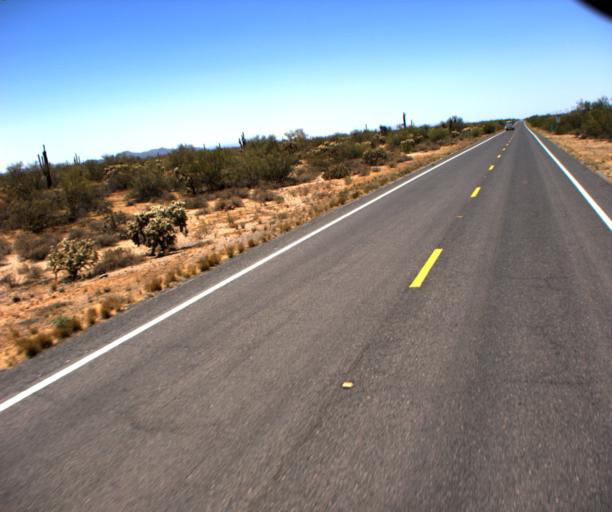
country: US
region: Arizona
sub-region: Pinal County
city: Florence
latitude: 32.8038
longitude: -111.1860
